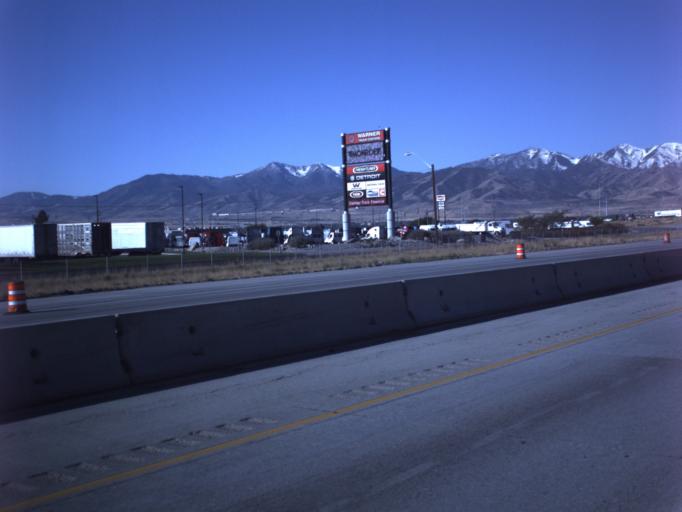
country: US
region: Utah
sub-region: Salt Lake County
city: West Valley City
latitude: 40.7259
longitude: -112.0183
